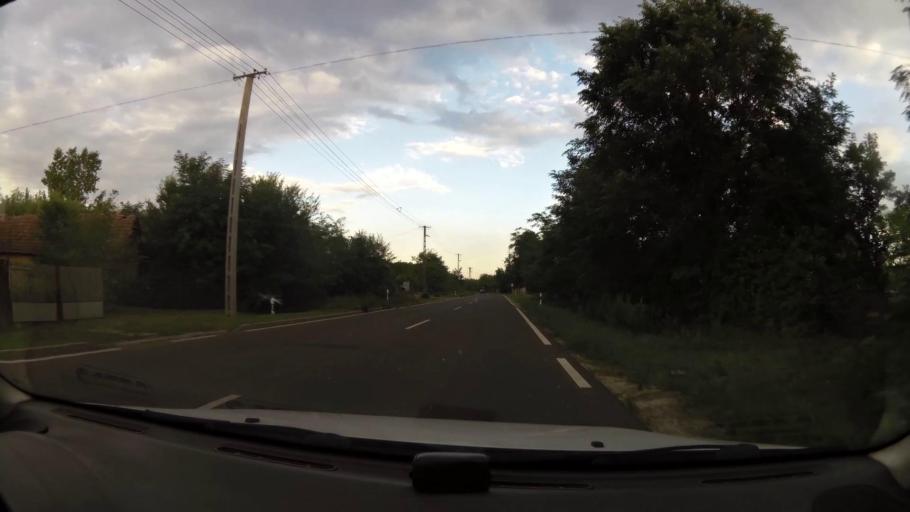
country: HU
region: Pest
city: Tapioszele
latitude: 47.3045
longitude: 19.8847
